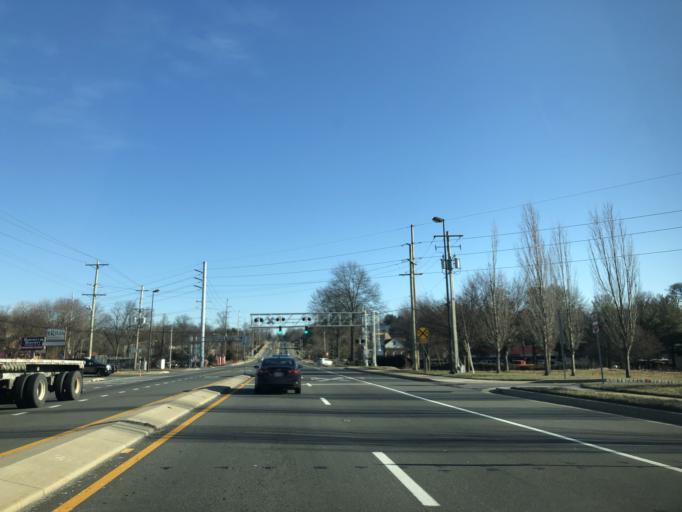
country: US
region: Delaware
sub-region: New Castle County
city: Hockessin
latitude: 39.7882
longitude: -75.6944
